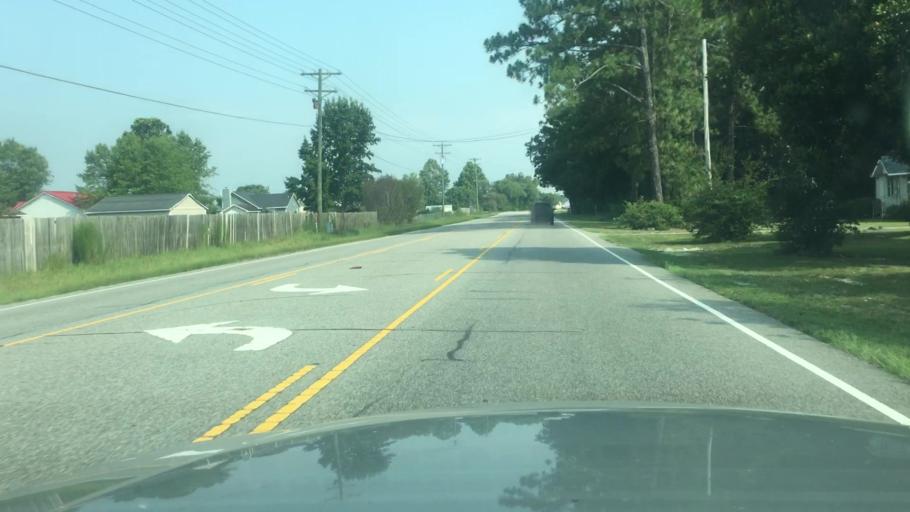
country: US
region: North Carolina
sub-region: Cumberland County
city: Hope Mills
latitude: 34.9162
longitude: -78.9087
